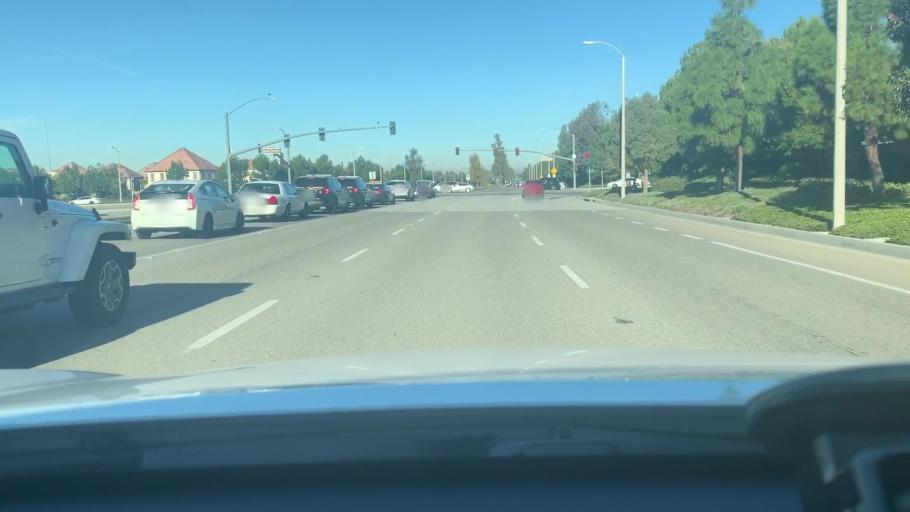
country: US
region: California
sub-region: Orange County
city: Lake Forest
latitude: 33.6866
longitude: -117.7480
